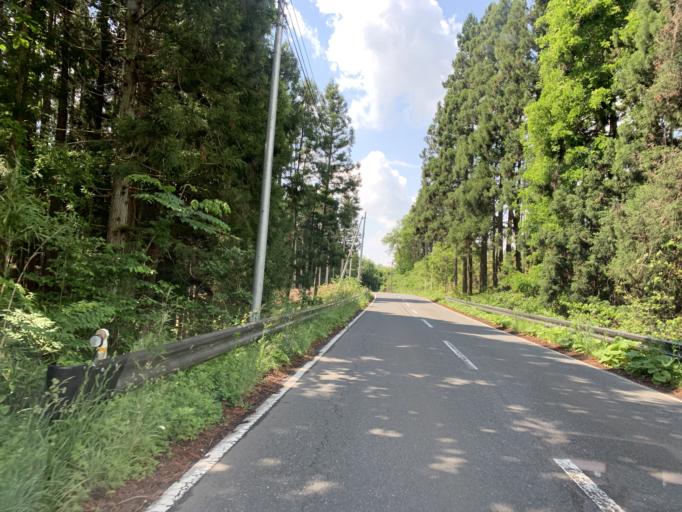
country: JP
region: Miyagi
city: Furukawa
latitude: 38.7060
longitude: 140.9331
